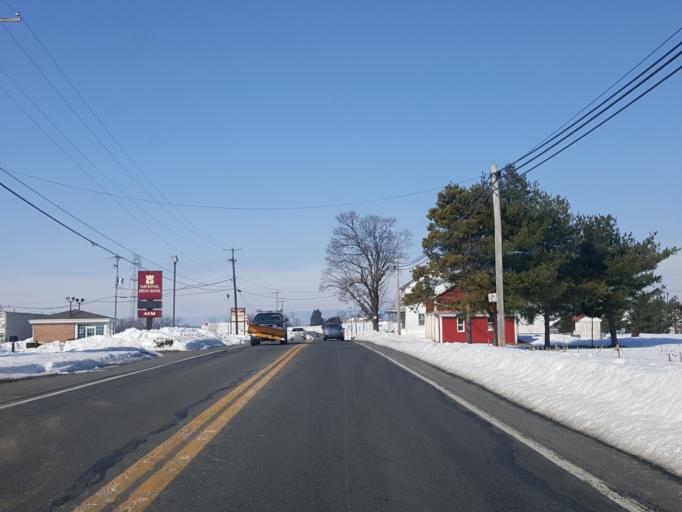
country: US
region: Pennsylvania
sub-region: Berks County
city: Robesonia
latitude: 40.4442
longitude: -76.1263
